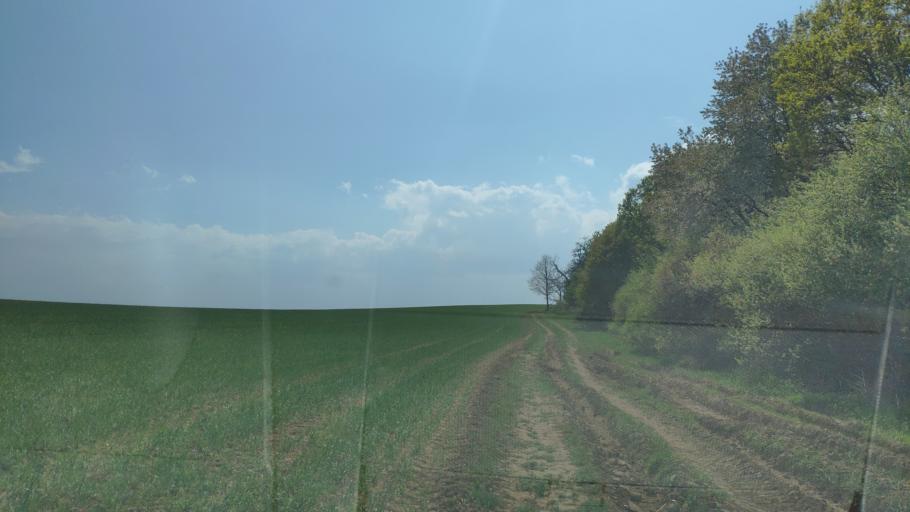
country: SK
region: Kosicky
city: Moldava nad Bodvou
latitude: 48.5485
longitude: 20.9477
